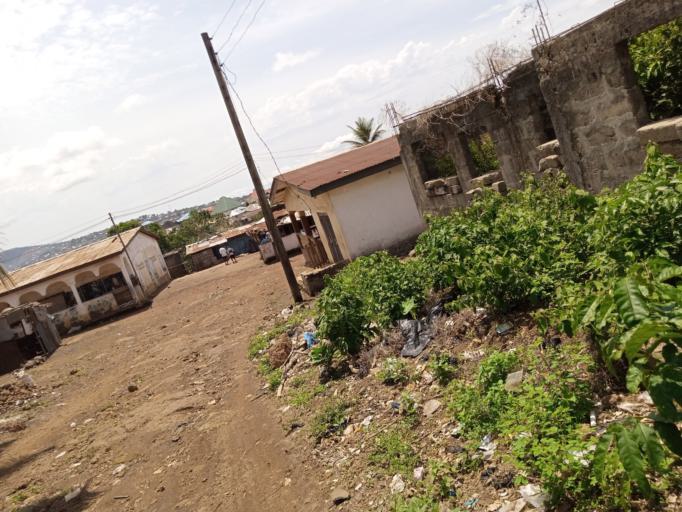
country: SL
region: Western Area
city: Hastings
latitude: 8.3835
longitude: -13.1386
